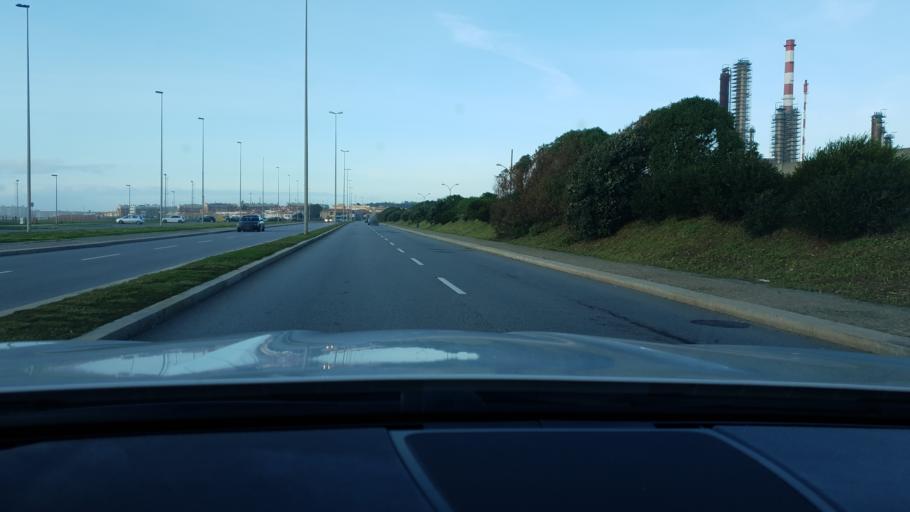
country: PT
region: Porto
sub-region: Matosinhos
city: Leca da Palmeira
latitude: 41.2158
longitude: -8.7129
